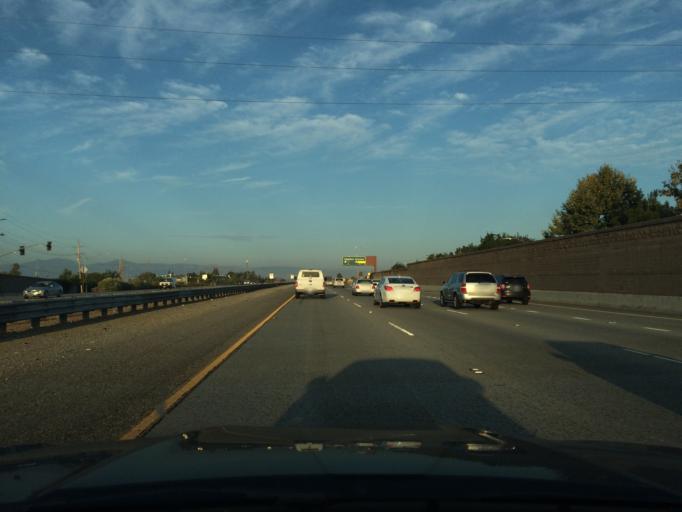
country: US
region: California
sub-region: Santa Clara County
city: Cambrian Park
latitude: 37.2505
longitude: -121.9137
